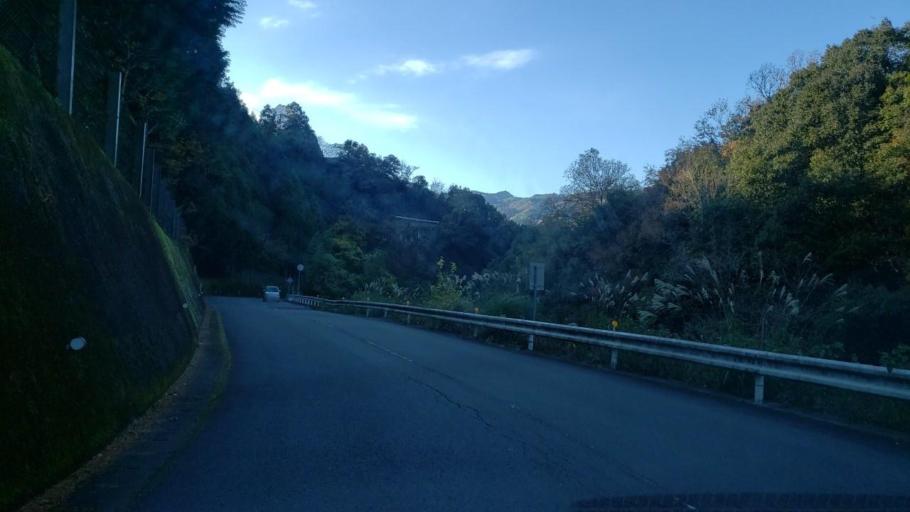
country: JP
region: Tokushima
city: Wakimachi
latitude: 34.0207
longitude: 134.0379
